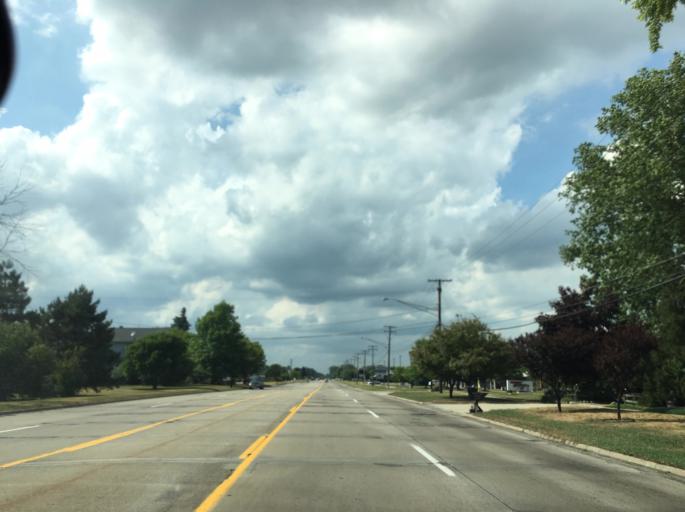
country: US
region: Michigan
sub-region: Macomb County
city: Fraser
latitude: 42.5467
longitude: -82.9573
